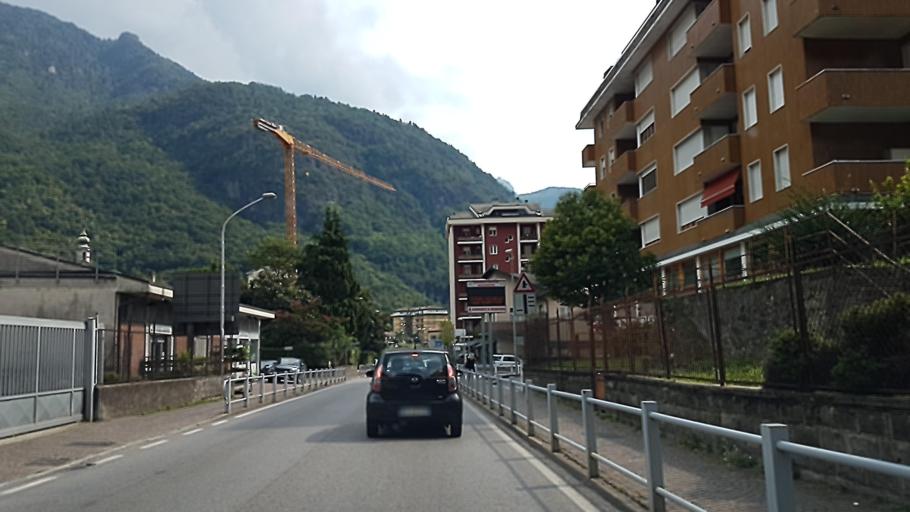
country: IT
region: Lombardy
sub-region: Provincia di Sondrio
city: Chiavenna
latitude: 46.3202
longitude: 9.3982
